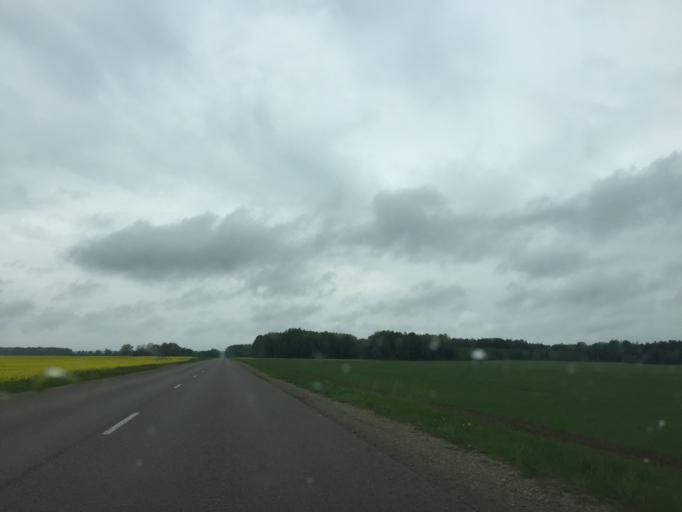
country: LV
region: Lielvarde
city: Lielvarde
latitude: 56.7908
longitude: 24.8070
